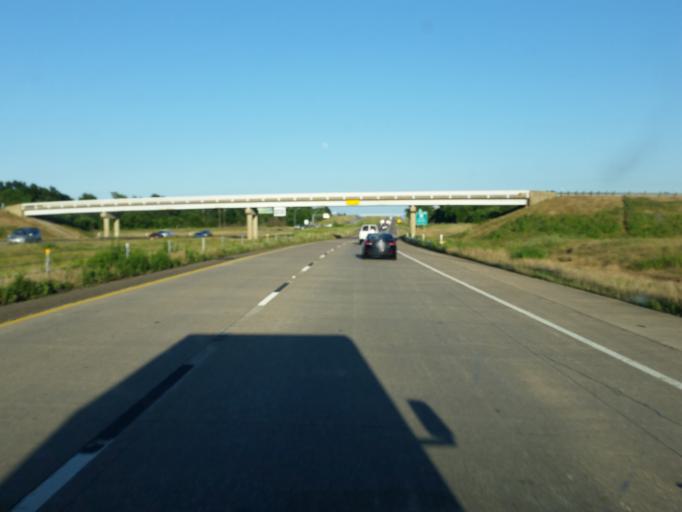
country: US
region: Texas
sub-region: Kaufman County
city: Terrell
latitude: 32.7129
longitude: -96.3020
